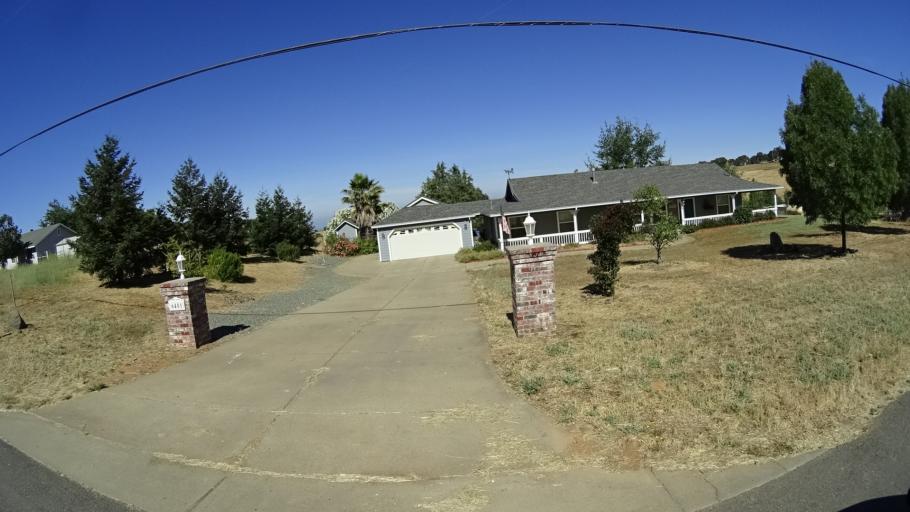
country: US
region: California
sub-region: Amador County
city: Jackson
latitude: 38.2634
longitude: -120.7641
